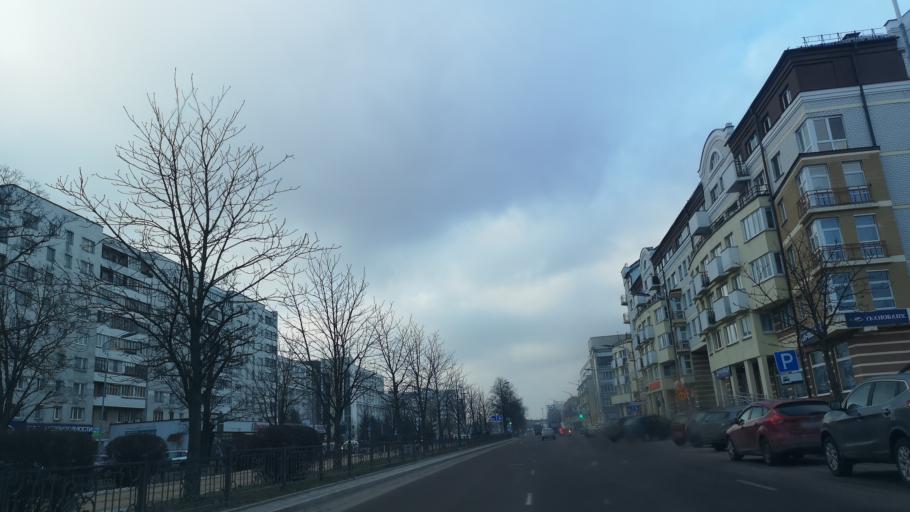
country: BY
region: Brest
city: Brest
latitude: 52.0967
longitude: 23.6972
